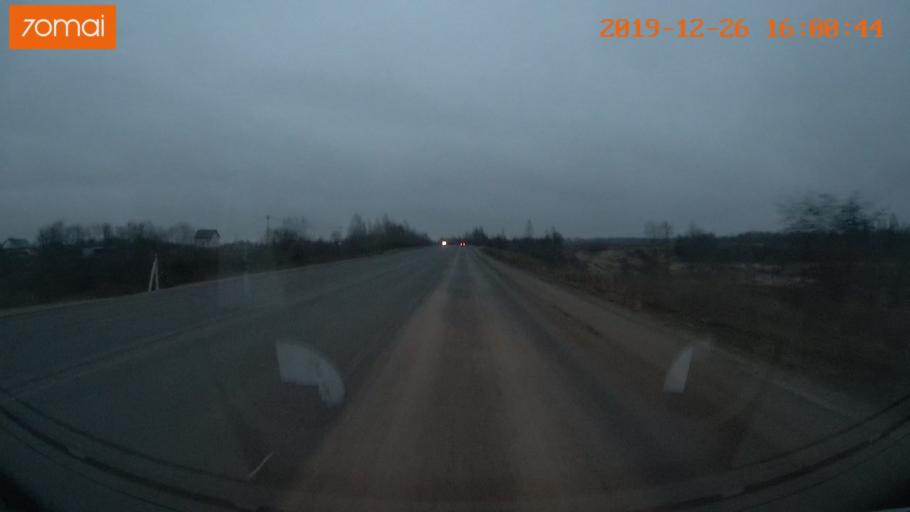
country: RU
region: Jaroslavl
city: Rybinsk
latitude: 58.0210
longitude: 38.8070
